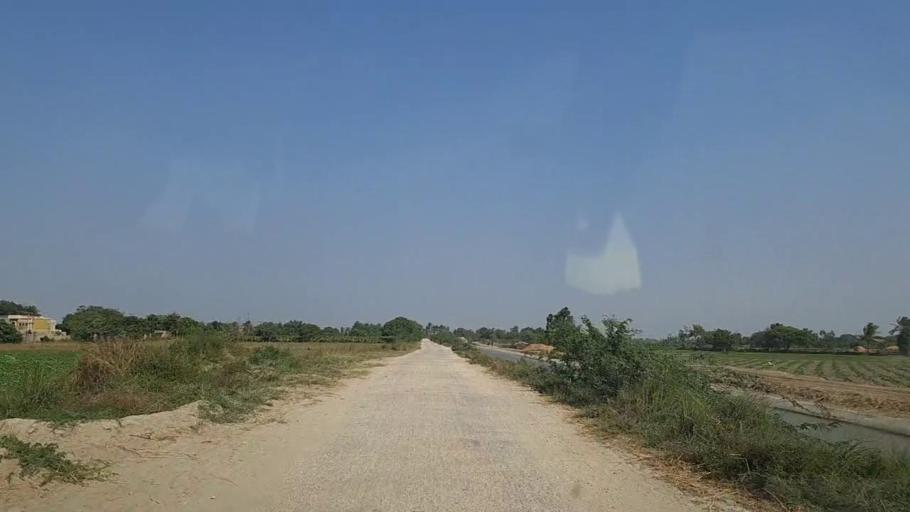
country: PK
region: Sindh
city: Mirpur Sakro
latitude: 24.5603
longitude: 67.8264
